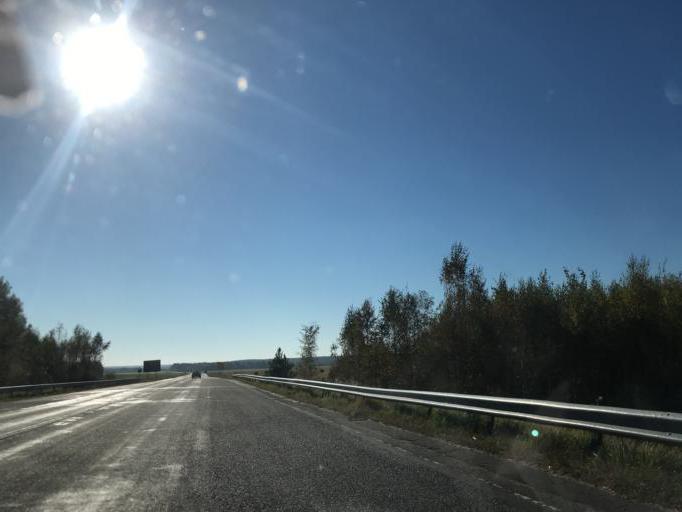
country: BY
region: Mogilev
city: Babruysk
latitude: 53.1020
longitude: 29.0574
